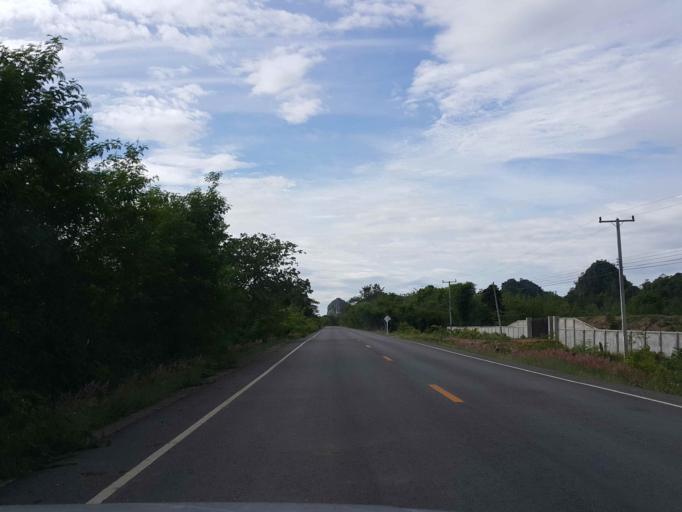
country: TH
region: Sukhothai
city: Thung Saliam
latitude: 17.2807
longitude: 99.5278
